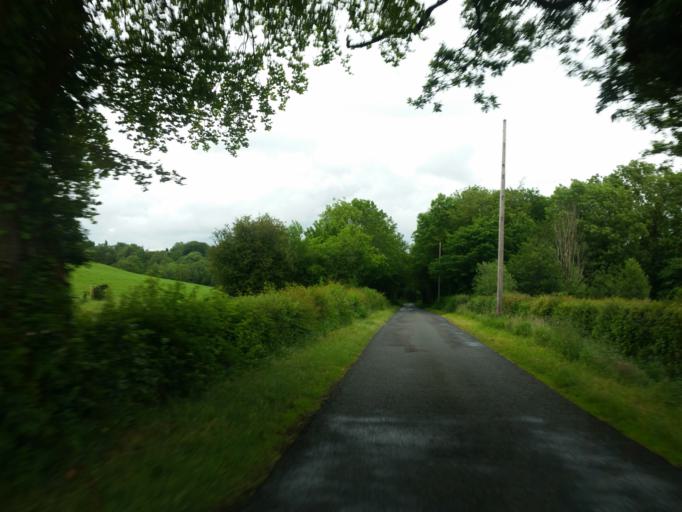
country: IE
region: Ulster
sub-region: County Monaghan
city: Clones
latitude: 54.1973
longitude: -7.2515
